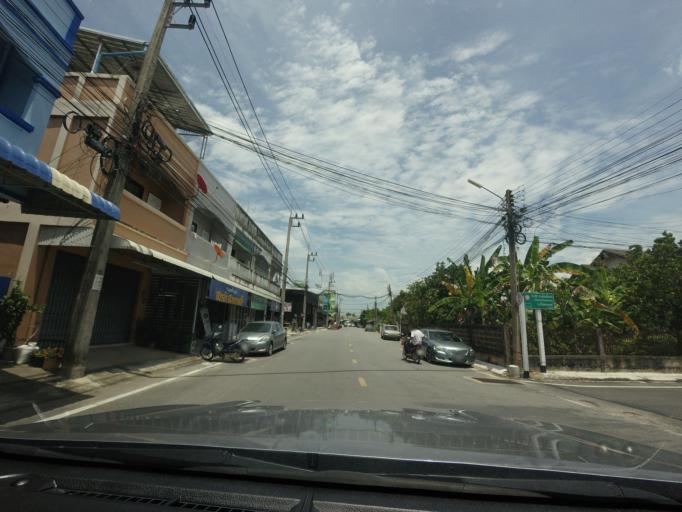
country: TH
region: Yala
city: Yala
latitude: 6.5447
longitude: 101.2940
